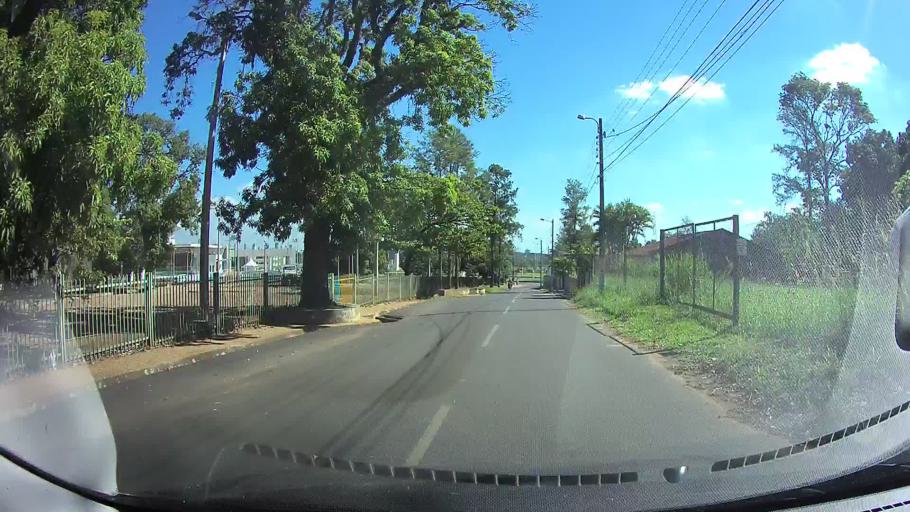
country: PY
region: Central
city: Fernando de la Mora
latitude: -25.2600
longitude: -57.5131
